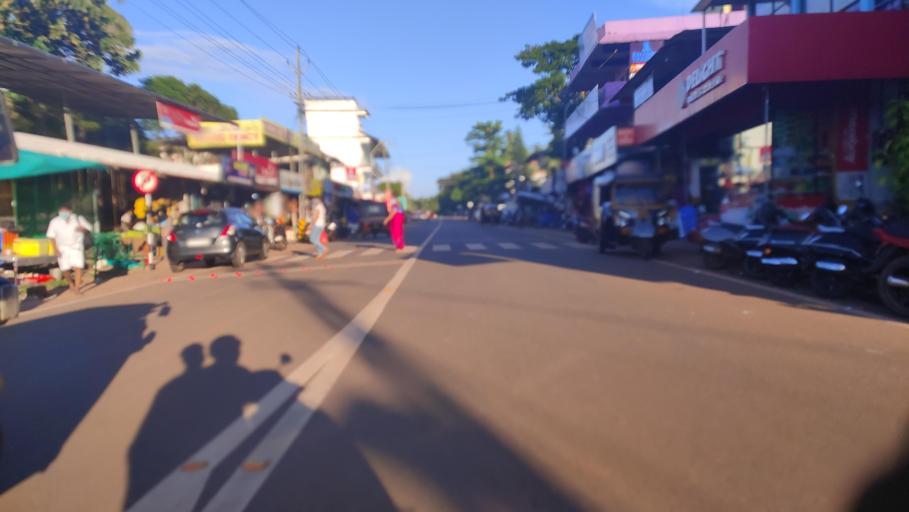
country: IN
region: Kerala
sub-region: Kasaragod District
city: Kasaragod
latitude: 12.4646
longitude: 75.0584
